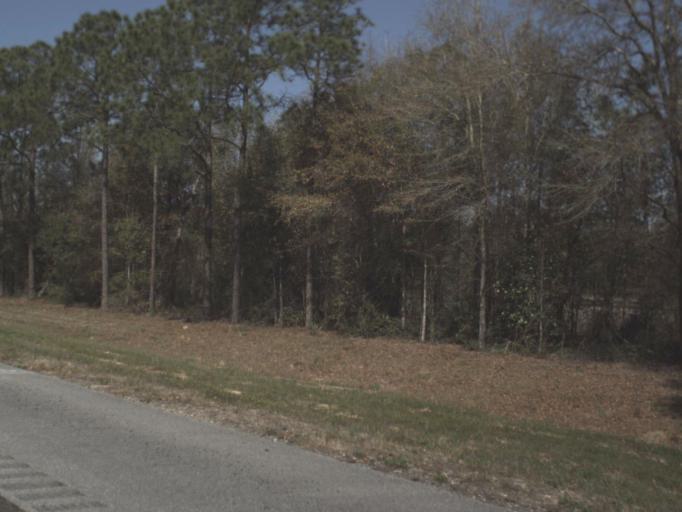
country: US
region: Florida
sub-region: Walton County
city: DeFuniak Springs
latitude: 30.7507
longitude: -86.2841
